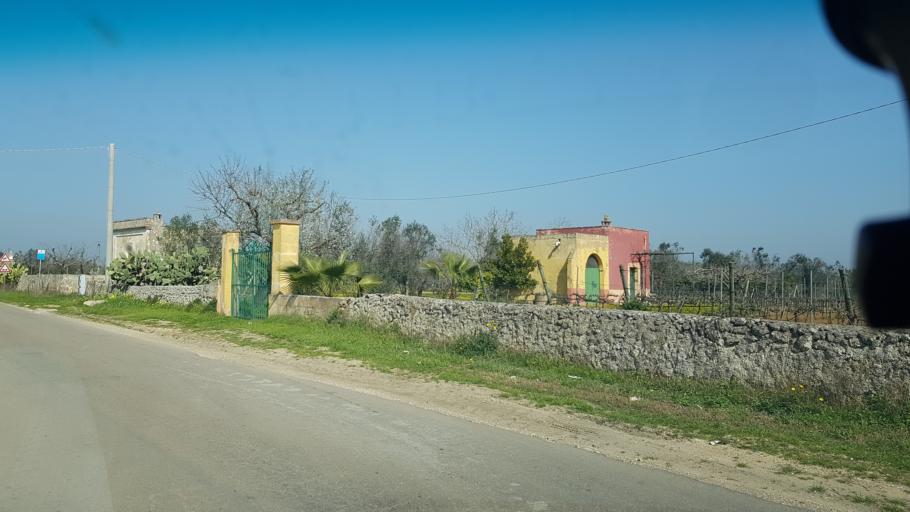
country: IT
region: Apulia
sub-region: Provincia di Lecce
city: Squinzano
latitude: 40.4488
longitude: 18.0412
